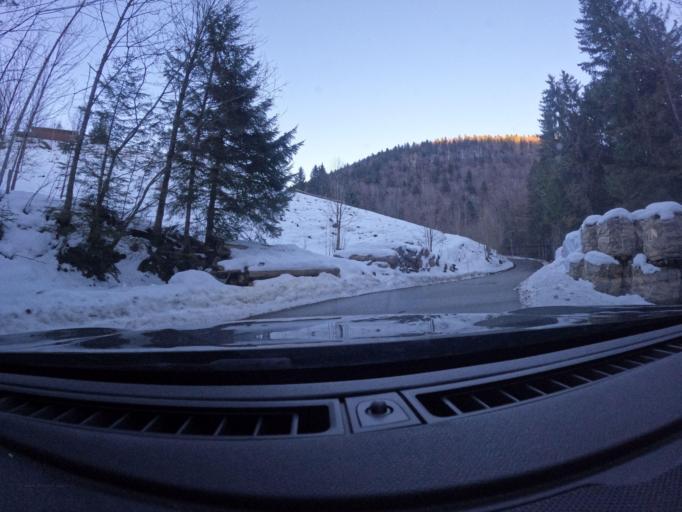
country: DE
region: Bavaria
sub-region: Upper Bavaria
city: Bergen
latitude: 47.7653
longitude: 12.6004
